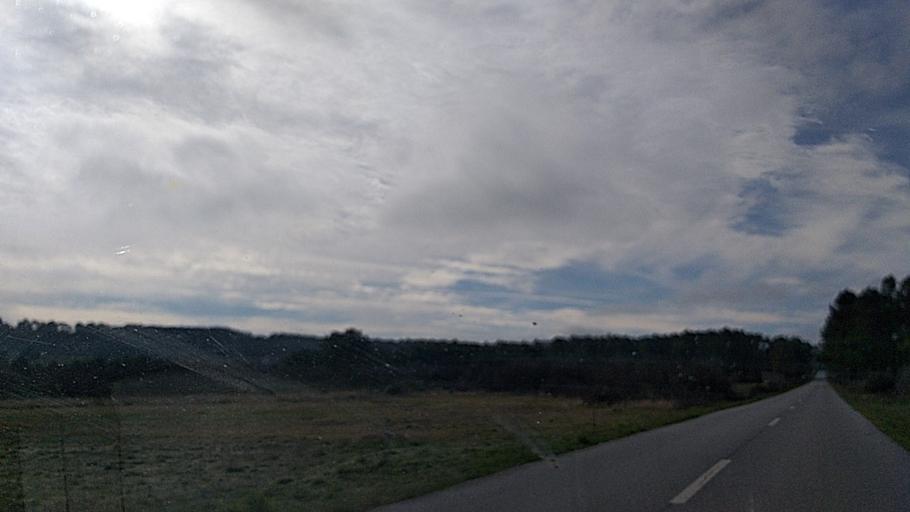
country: PT
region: Guarda
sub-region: Fornos de Algodres
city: Fornos de Algodres
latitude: 40.6694
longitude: -7.5292
